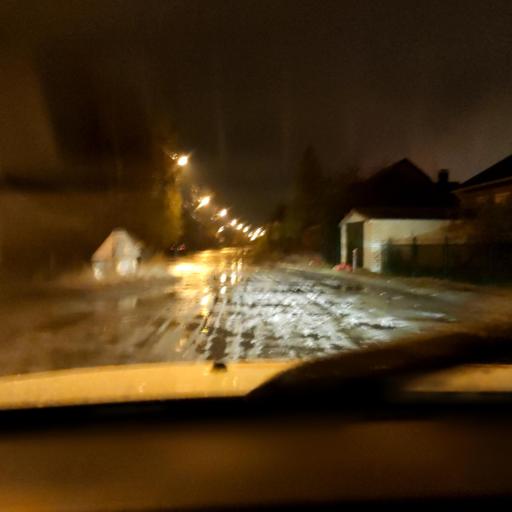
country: RU
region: Voronezj
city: Somovo
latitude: 51.7414
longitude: 39.3236
